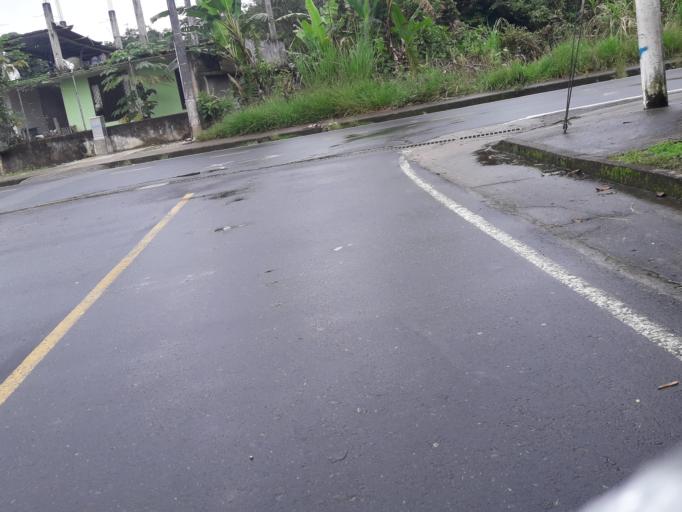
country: EC
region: Napo
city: Tena
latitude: -0.9678
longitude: -77.8559
